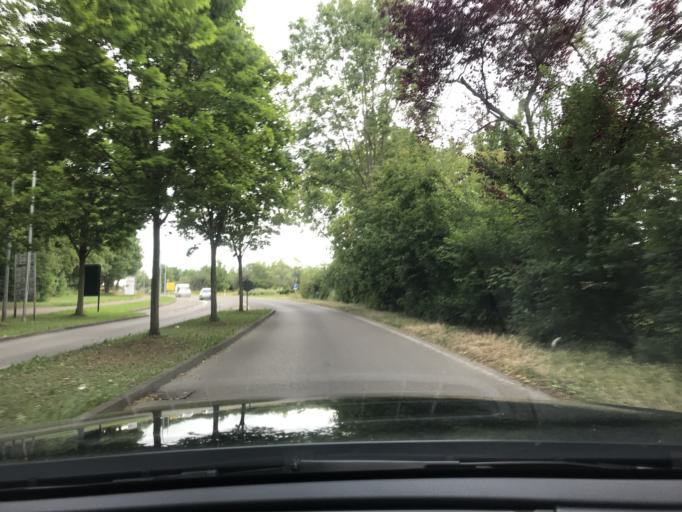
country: DE
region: Baden-Wuerttemberg
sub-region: Regierungsbezirk Stuttgart
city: Stuttgart Muehlhausen
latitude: 48.8323
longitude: 9.2576
